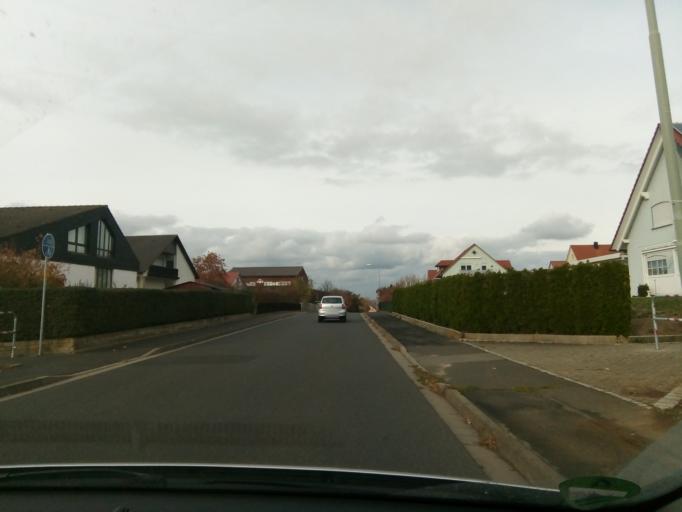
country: DE
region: Bavaria
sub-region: Regierungsbezirk Unterfranken
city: Gerolzhofen
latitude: 49.8931
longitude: 10.3528
